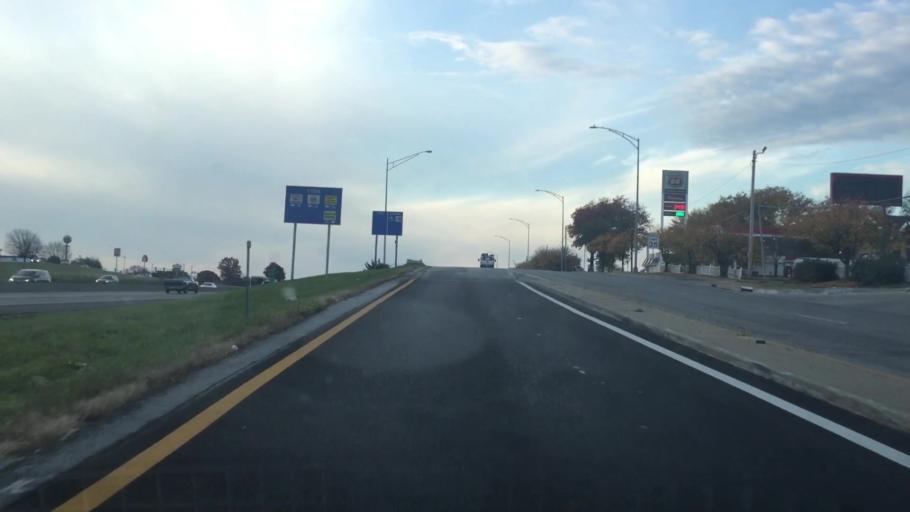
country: US
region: Missouri
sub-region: Jackson County
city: Grandview
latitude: 38.8926
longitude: -94.5253
